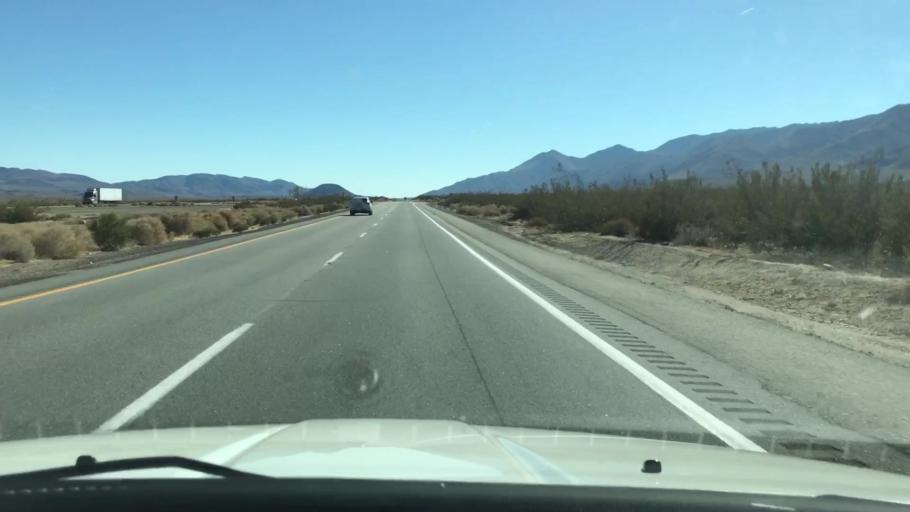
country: US
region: California
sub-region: Kern County
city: Inyokern
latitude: 36.0828
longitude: -117.9598
